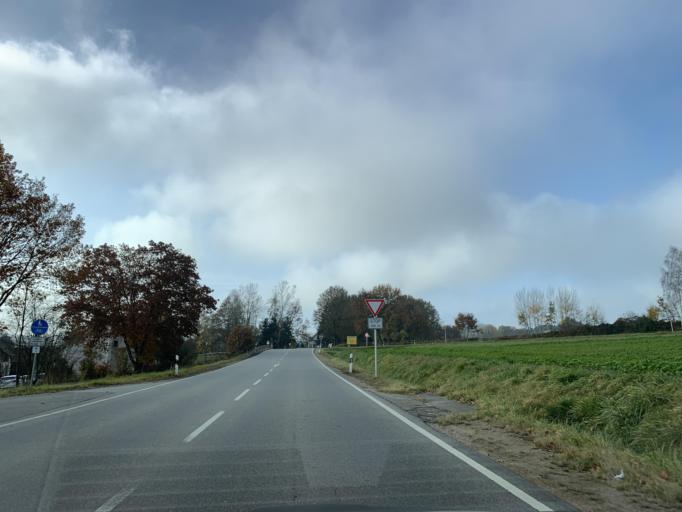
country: DE
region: Bavaria
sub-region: Upper Palatinate
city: Bruck in der Oberpfalz
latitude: 49.2651
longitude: 12.2966
